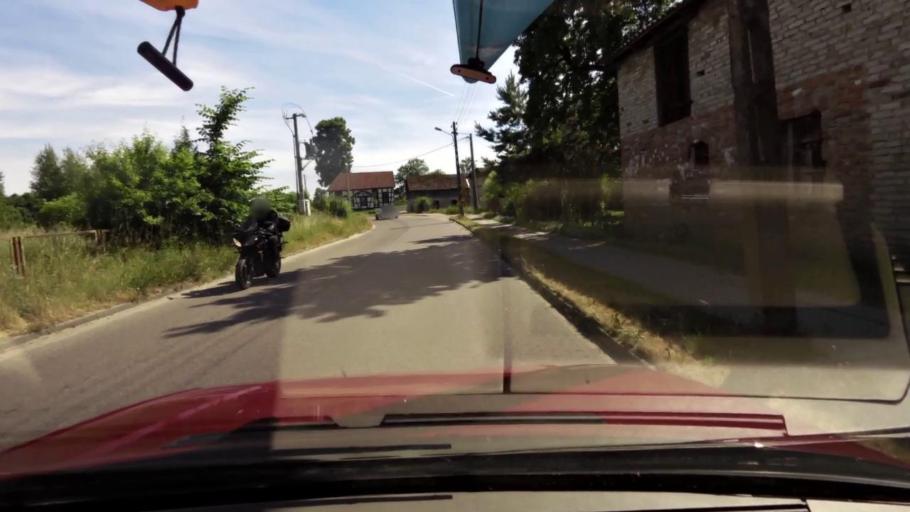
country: PL
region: Pomeranian Voivodeship
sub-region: Powiat slupski
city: Kobylnica
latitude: 54.3545
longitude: 16.9680
